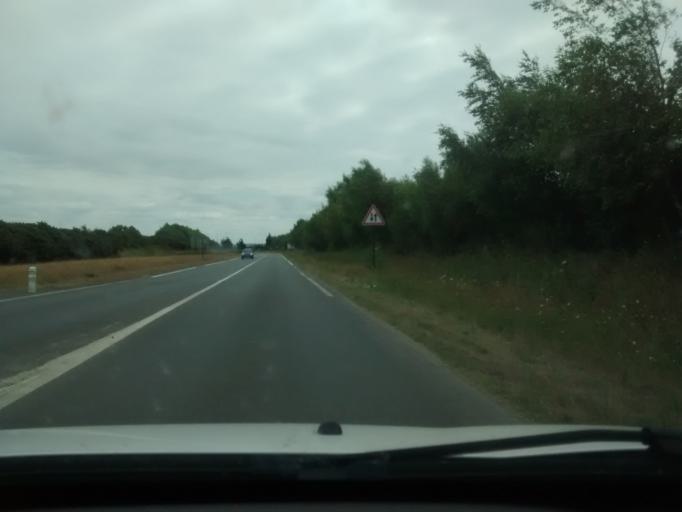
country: FR
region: Brittany
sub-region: Departement des Cotes-d'Armor
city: Saint-Quay-Perros
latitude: 48.7553
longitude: -3.4483
